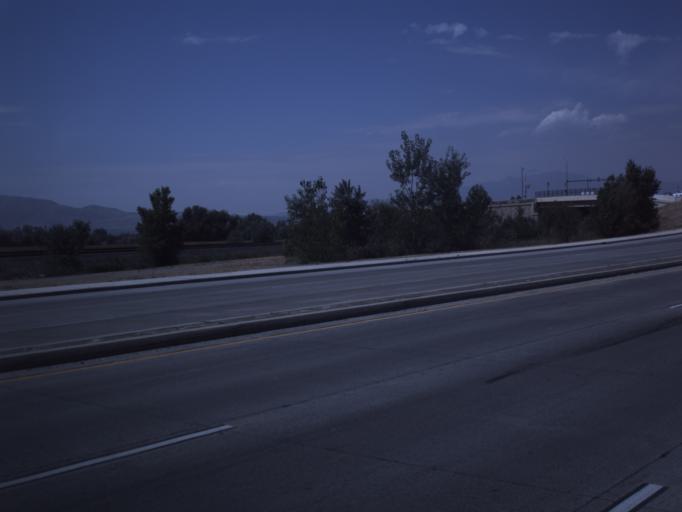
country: US
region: Utah
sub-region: Utah County
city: Lehi
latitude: 40.3772
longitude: -111.8285
